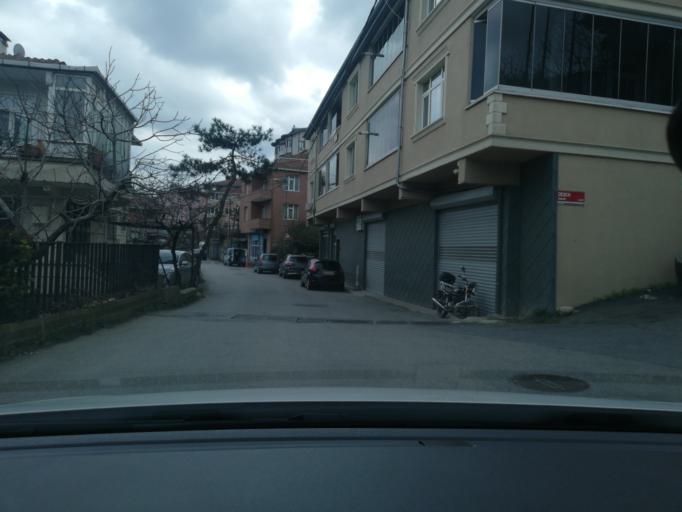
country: TR
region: Istanbul
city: UEskuedar
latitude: 41.0744
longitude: 29.0682
